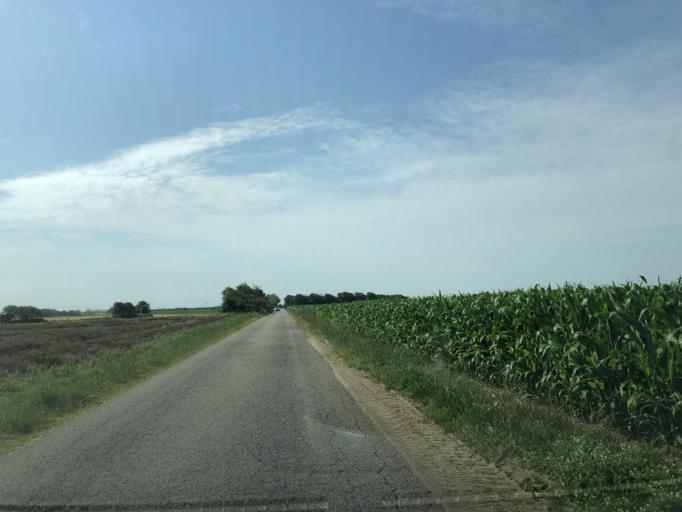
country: DK
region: Central Jutland
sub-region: Lemvig Kommune
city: Lemvig
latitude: 56.4322
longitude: 8.2722
